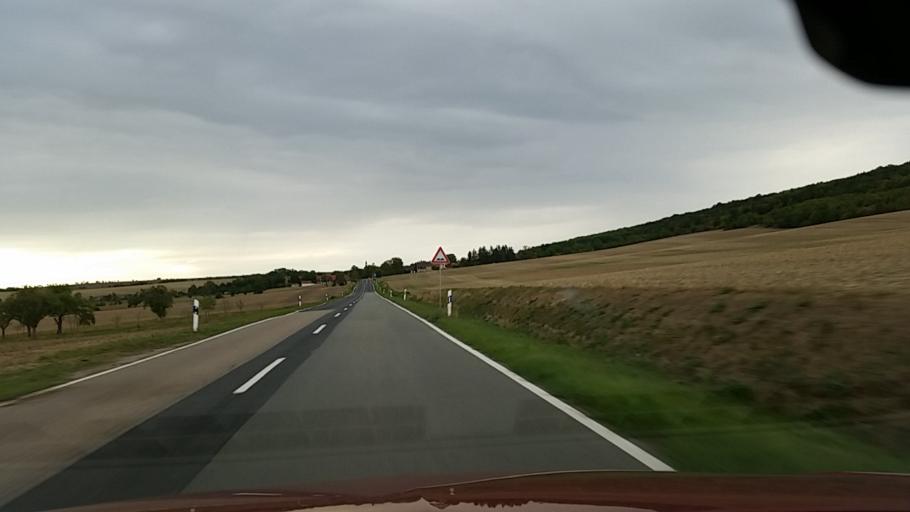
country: DE
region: Saxony-Anhalt
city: Eckartsberga
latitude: 51.1231
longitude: 11.5404
